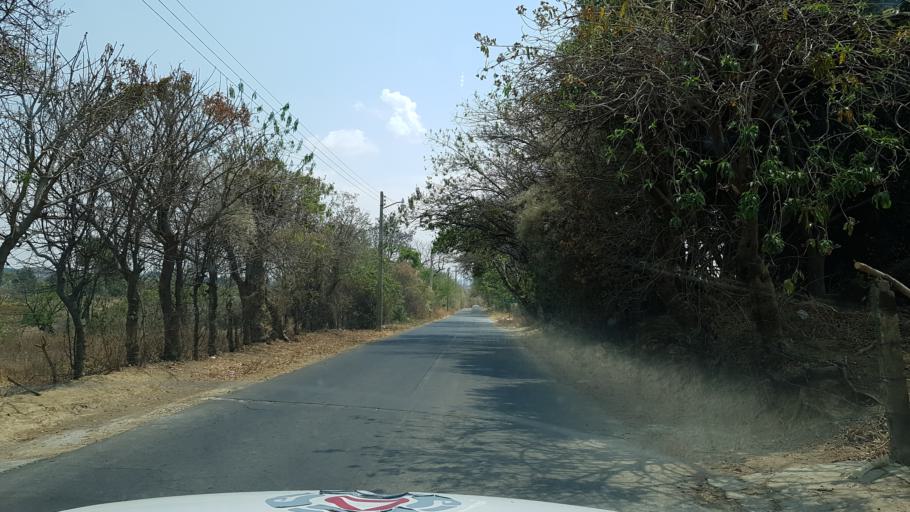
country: MX
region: Morelos
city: Ocuituco
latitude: 18.8969
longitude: -98.8078
